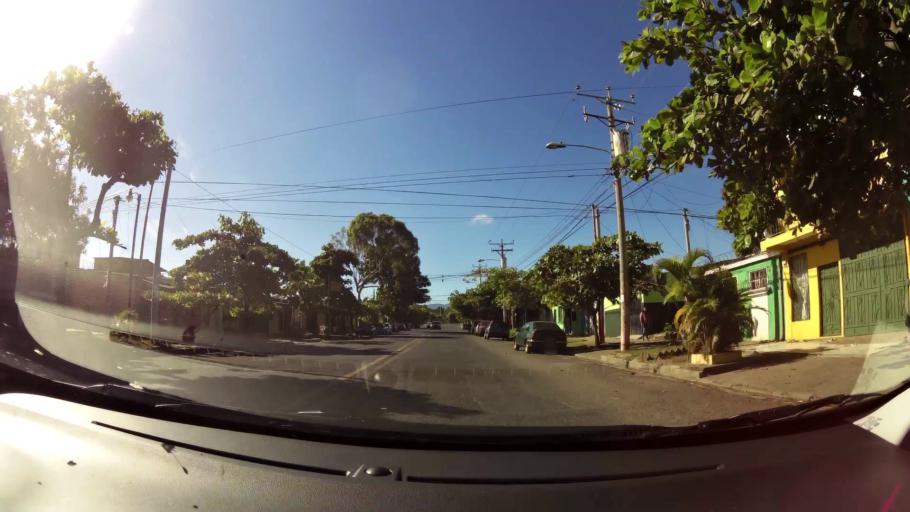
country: SV
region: Santa Ana
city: Santa Ana
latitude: 13.9665
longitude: -89.5744
